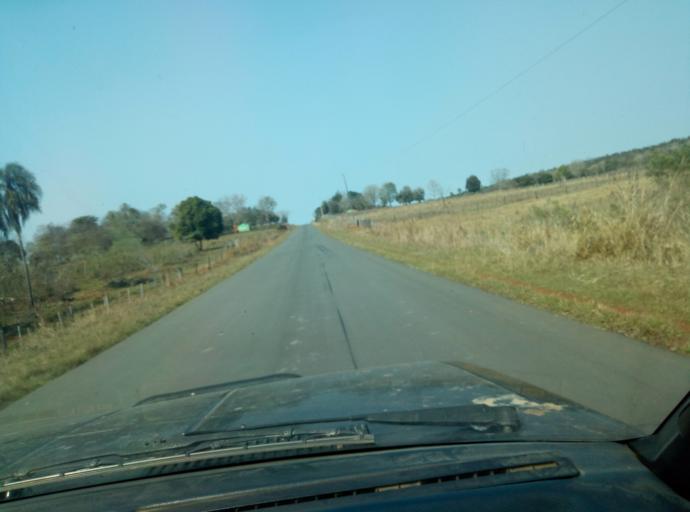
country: PY
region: Caaguazu
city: Carayao
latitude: -25.2592
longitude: -56.2879
